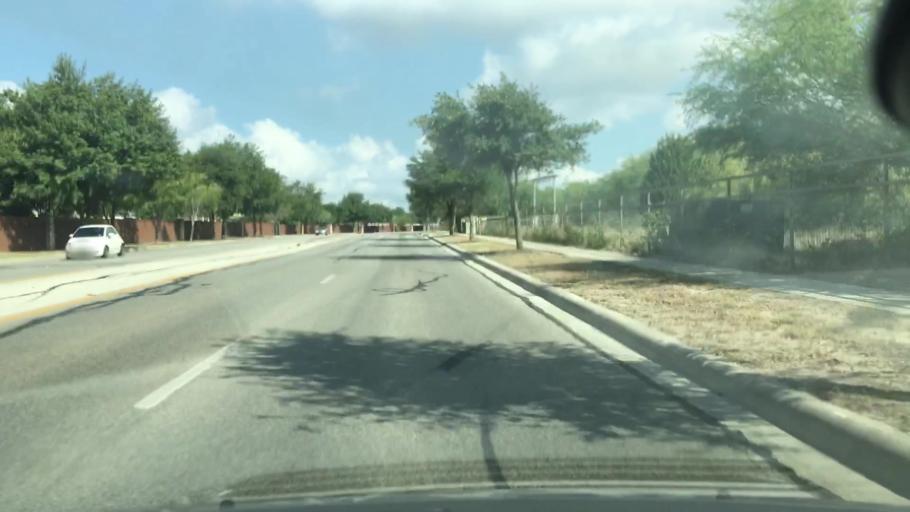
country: US
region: Texas
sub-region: Guadalupe County
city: Cibolo
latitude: 29.5794
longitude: -98.2453
